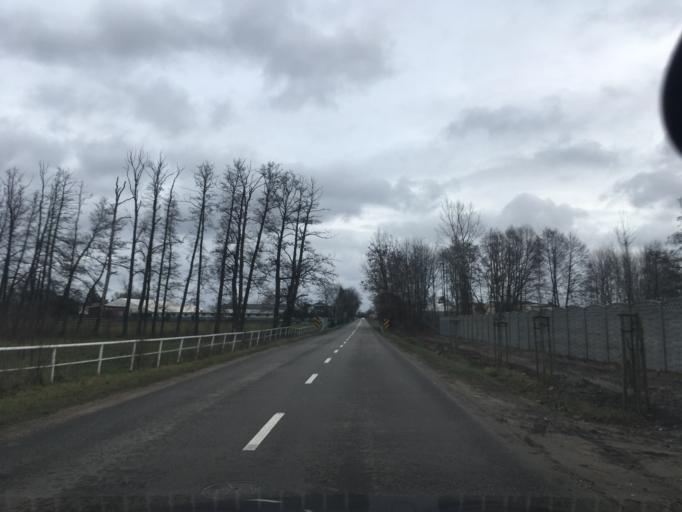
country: PL
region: Masovian Voivodeship
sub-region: Powiat piaseczynski
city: Lesznowola
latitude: 52.1206
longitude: 20.9370
